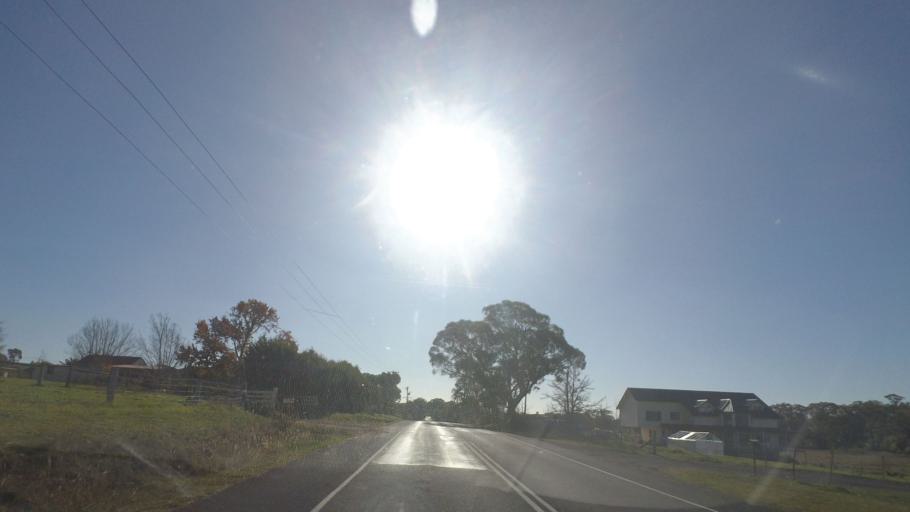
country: AU
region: Victoria
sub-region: Greater Bendigo
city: Kennington
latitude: -36.8976
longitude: 144.3143
